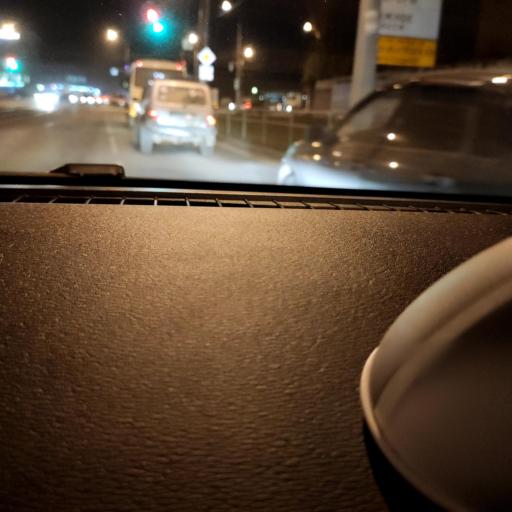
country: RU
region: Samara
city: Samara
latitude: 53.1961
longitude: 50.2493
